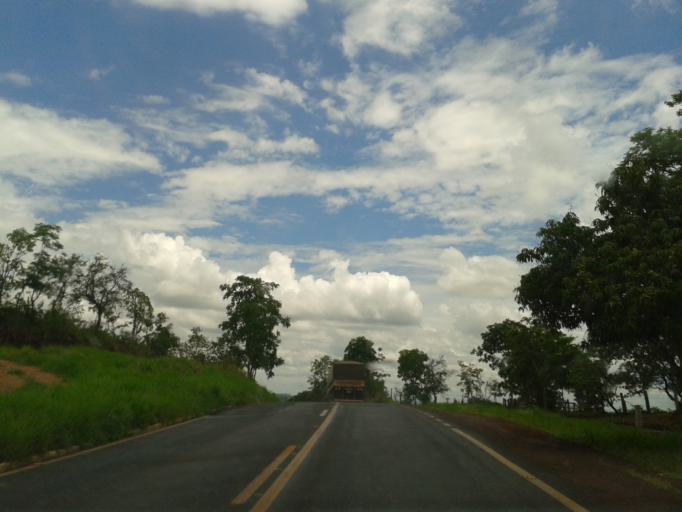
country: BR
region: Minas Gerais
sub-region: Ituiutaba
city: Ituiutaba
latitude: -19.1877
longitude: -49.7814
